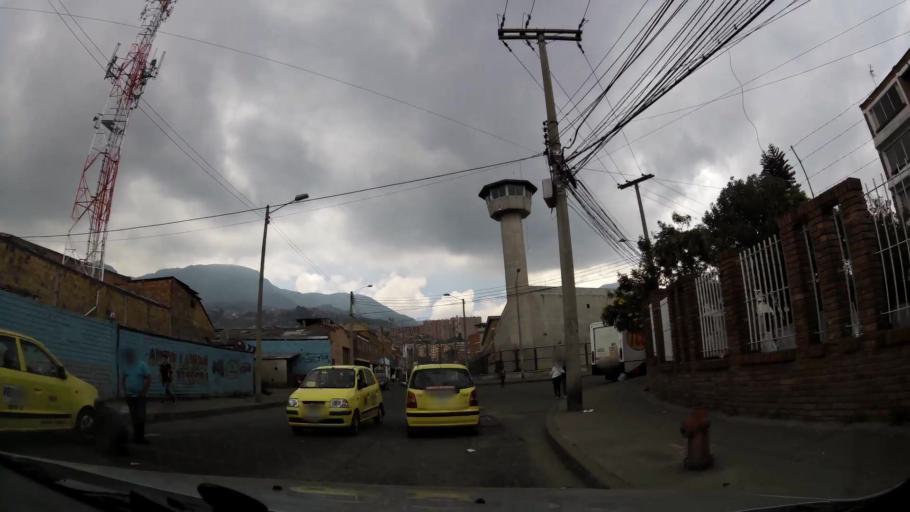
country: CO
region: Bogota D.C.
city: Bogota
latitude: 4.5867
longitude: -74.0855
